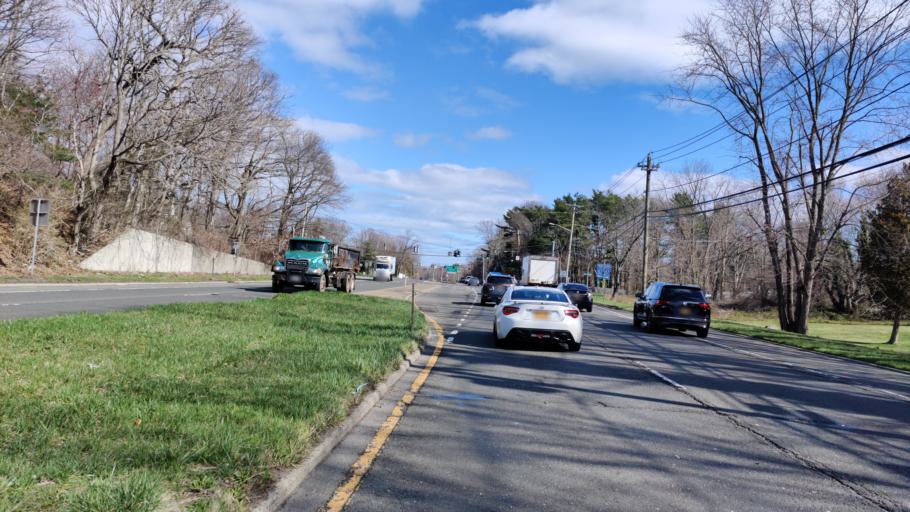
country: US
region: New York
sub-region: Suffolk County
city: Dix Hills
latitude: 40.8102
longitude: -73.3422
